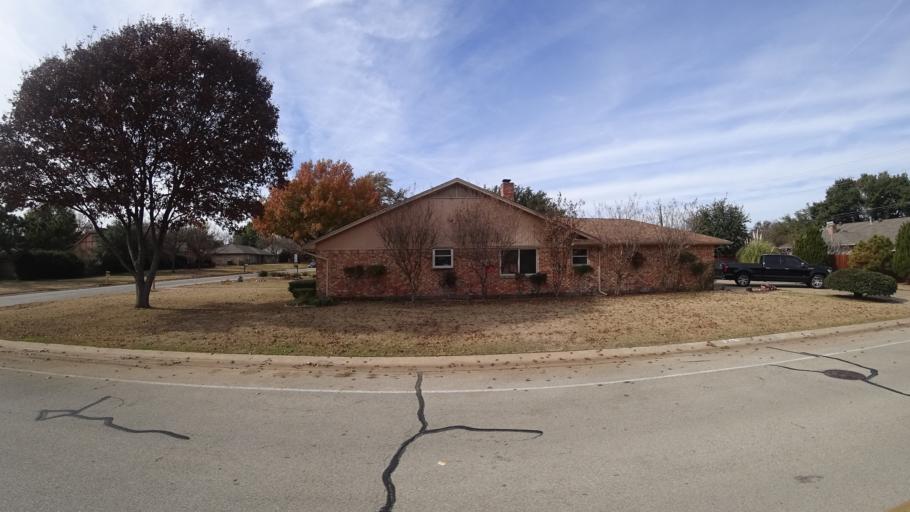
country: US
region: Texas
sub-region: Denton County
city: Highland Village
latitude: 33.0814
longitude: -97.0452
